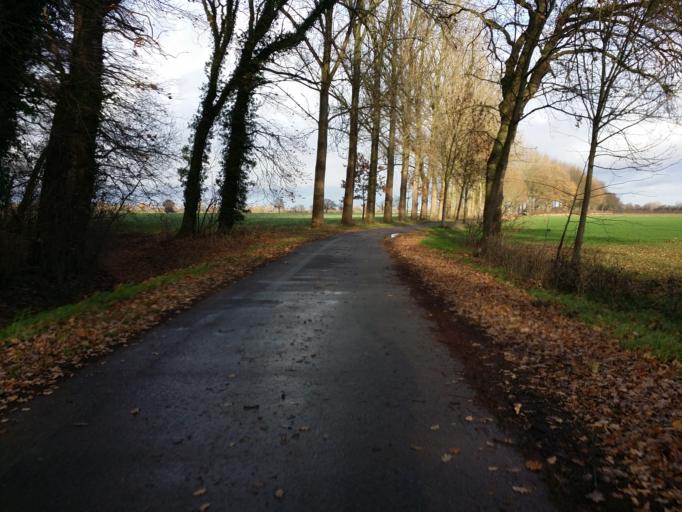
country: DE
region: Lower Saxony
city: Riede
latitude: 52.9782
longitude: 8.9728
